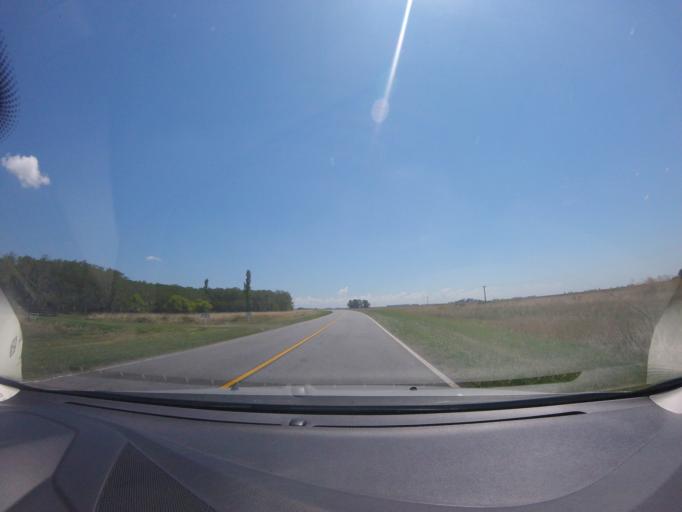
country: AR
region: Buenos Aires
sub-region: Partido de Rauch
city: Rauch
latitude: -36.5236
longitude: -59.0353
